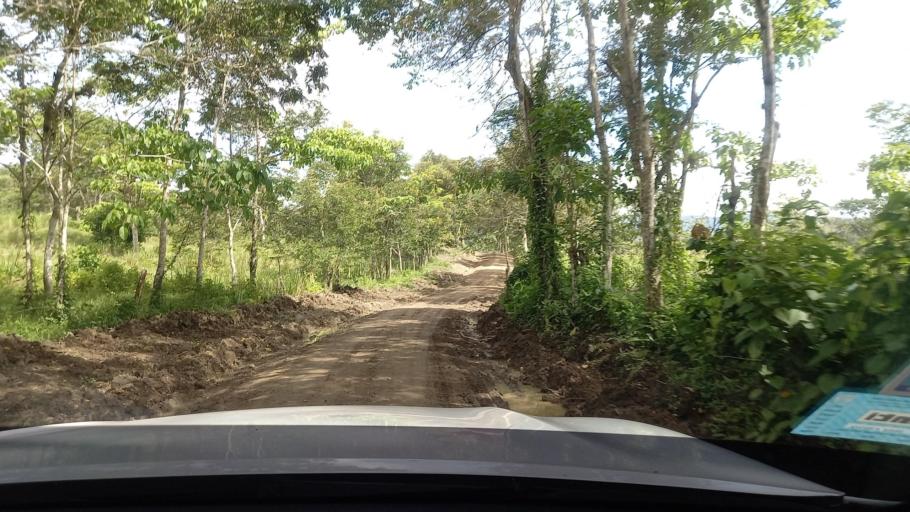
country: NI
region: Jinotega
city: San Jose de Bocay
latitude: 13.3838
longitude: -85.6884
